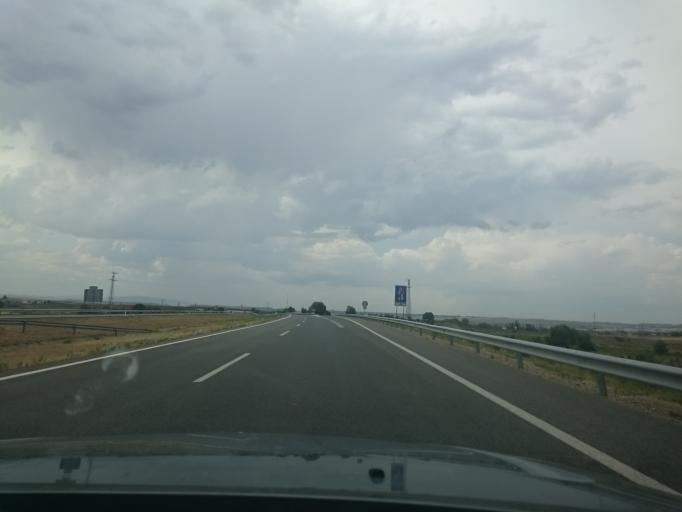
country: ES
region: Navarre
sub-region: Provincia de Navarra
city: Murchante
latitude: 42.0285
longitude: -1.6287
